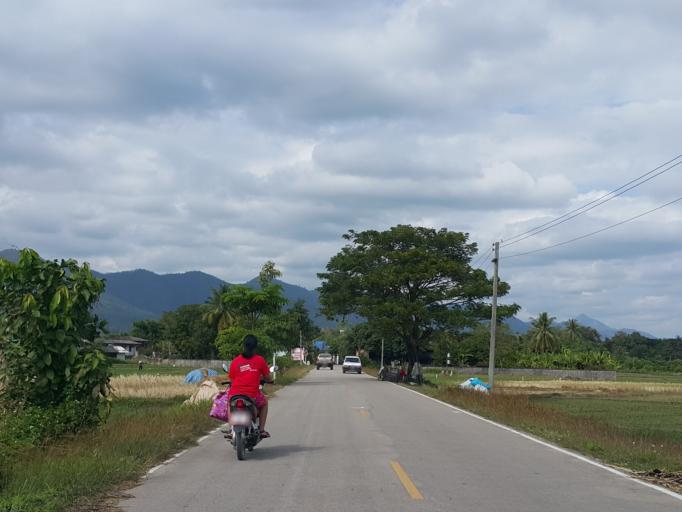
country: TH
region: Lampang
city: Chae Hom
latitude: 18.5567
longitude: 99.4584
